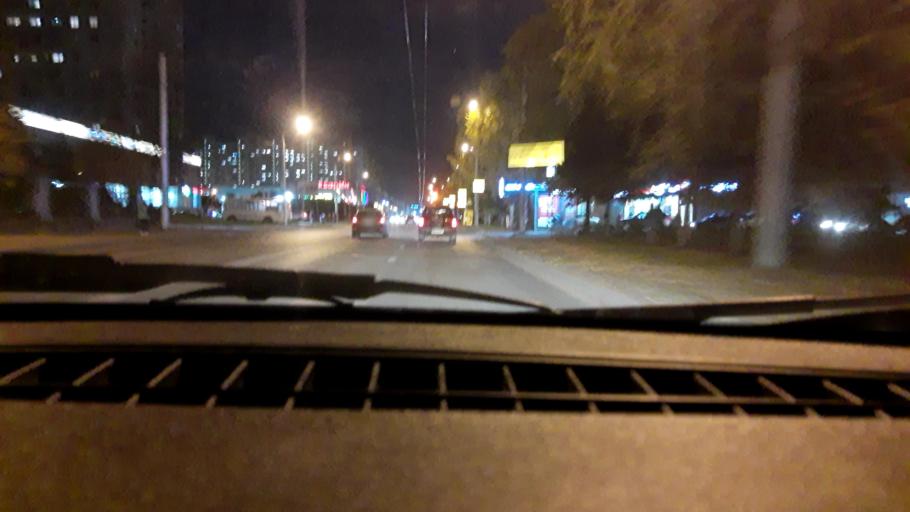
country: RU
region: Bashkortostan
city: Ufa
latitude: 54.7826
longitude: 56.1311
